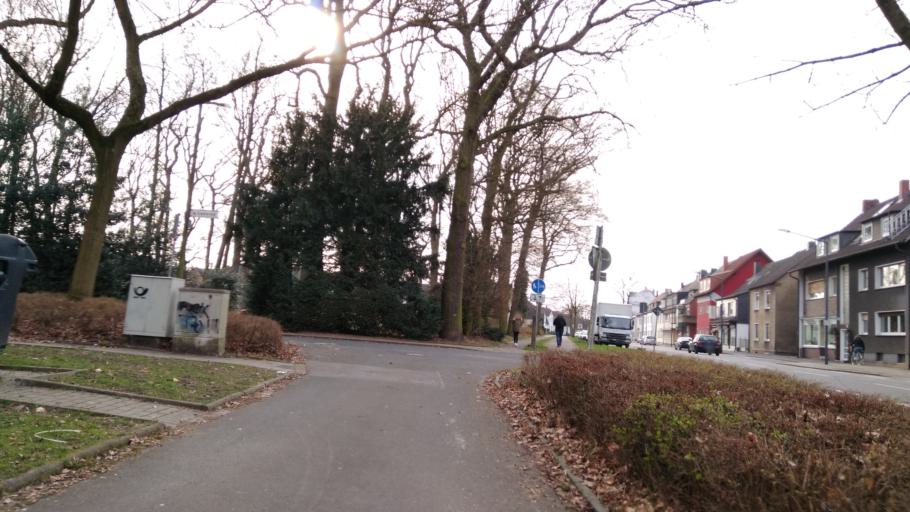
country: DE
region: North Rhine-Westphalia
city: Herten
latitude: 51.6141
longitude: 7.1299
